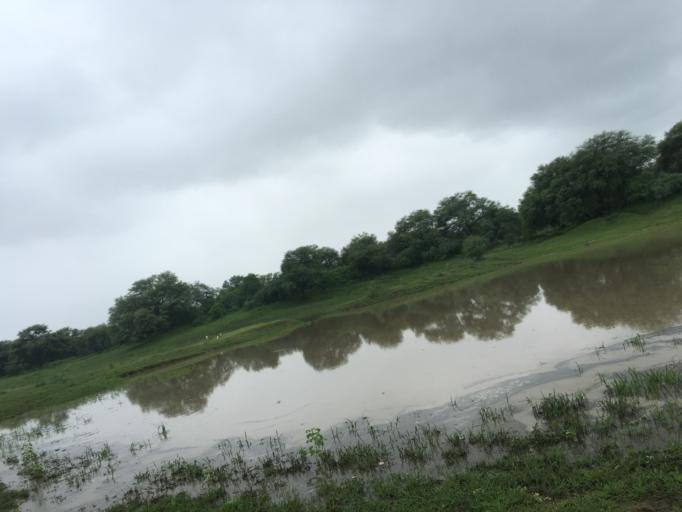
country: IN
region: Gujarat
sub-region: Mahesana
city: Kadi
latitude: 23.1620
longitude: 72.3787
